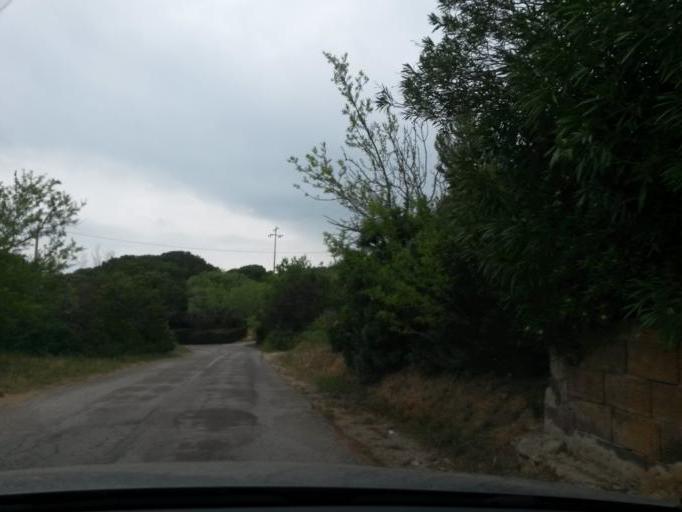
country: IT
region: Tuscany
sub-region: Provincia di Livorno
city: Capoliveri
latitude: 42.7386
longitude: 10.3722
